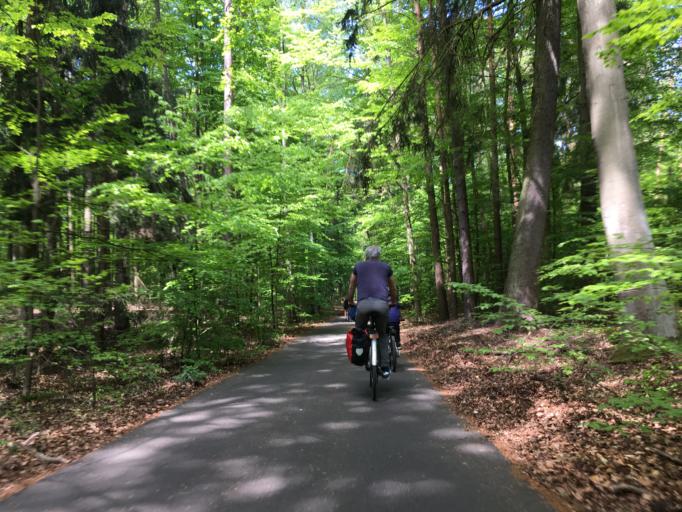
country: DE
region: Brandenburg
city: Wandlitz
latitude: 52.7382
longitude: 13.4976
